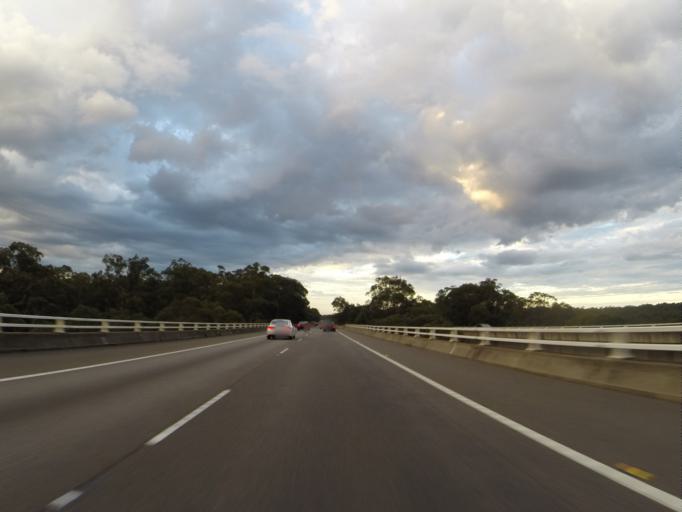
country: AU
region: New South Wales
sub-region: Wollondilly
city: Douglas Park
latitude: -34.2106
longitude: 150.6903
